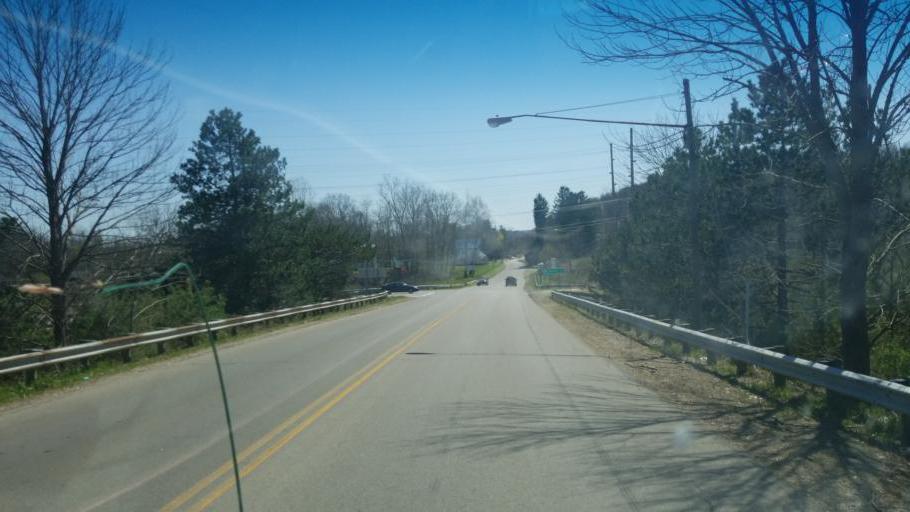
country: US
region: Ohio
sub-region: Richland County
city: Lincoln Heights
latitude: 40.7781
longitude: -82.4953
